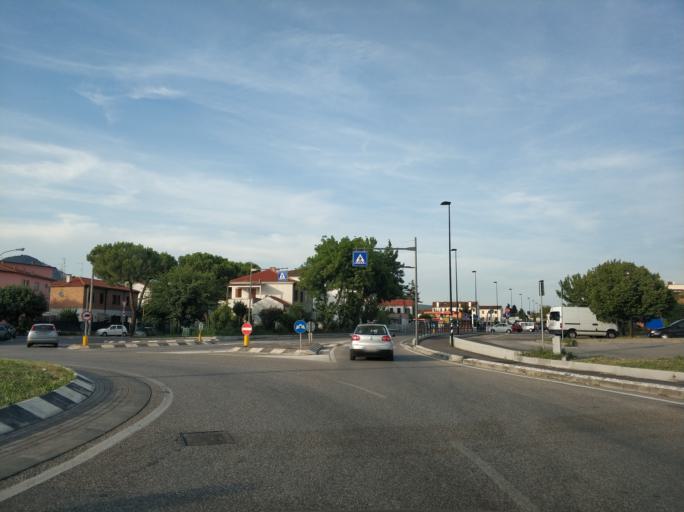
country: IT
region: Veneto
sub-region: Provincia di Padova
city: Este
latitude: 45.2224
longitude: 11.6594
